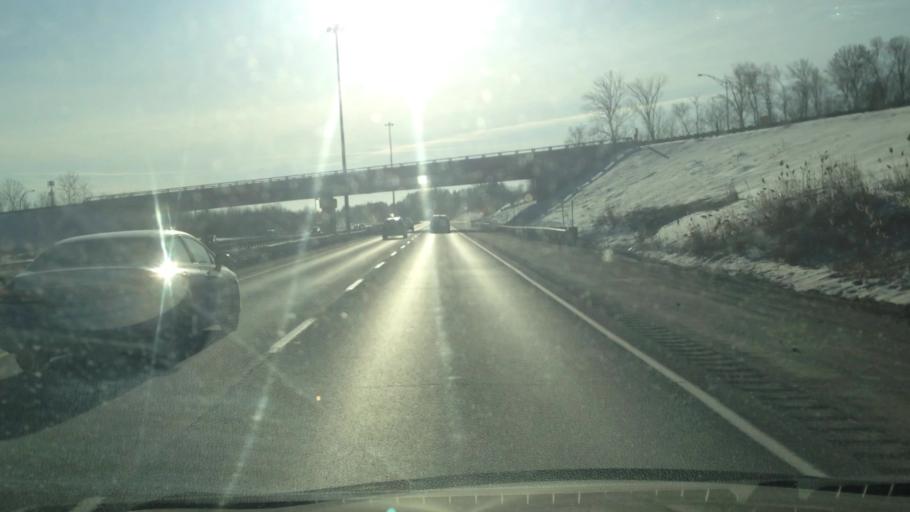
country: CA
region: Quebec
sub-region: Laurentides
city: Prevost
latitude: 45.8416
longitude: -74.0692
